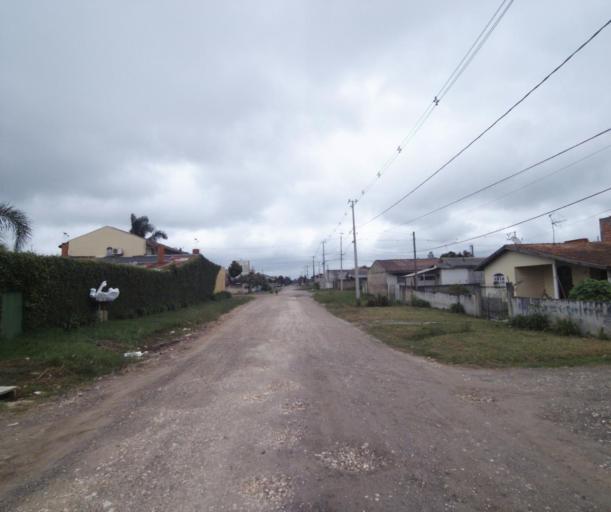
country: BR
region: Parana
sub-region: Quatro Barras
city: Quatro Barras
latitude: -25.3588
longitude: -49.0994
